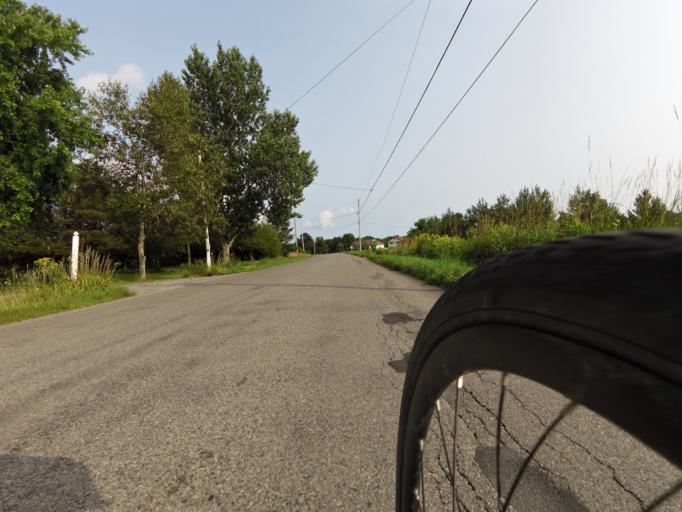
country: CA
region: Ontario
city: Quinte West
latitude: 44.0533
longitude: -77.6363
